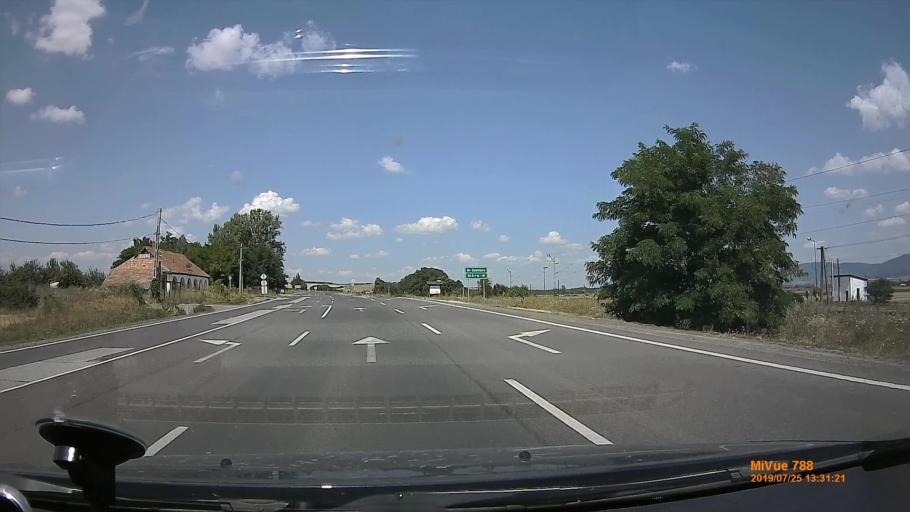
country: HU
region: Borsod-Abauj-Zemplen
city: Encs
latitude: 48.3624
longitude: 21.1395
